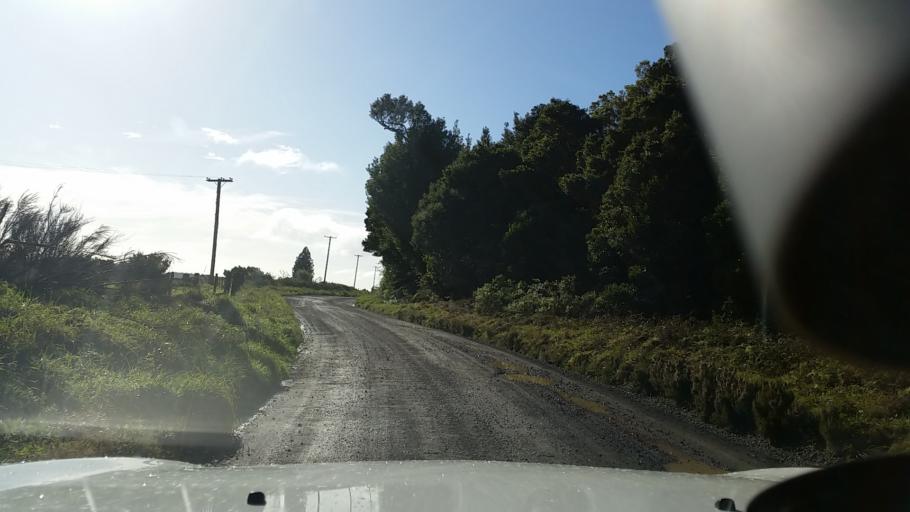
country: NZ
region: Bay of Plenty
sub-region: Rotorua District
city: Rotorua
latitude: -38.0198
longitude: 176.4637
